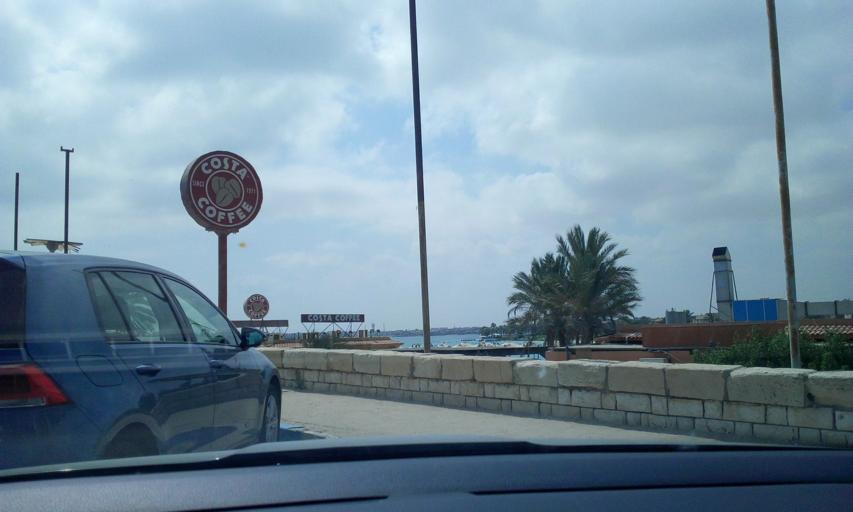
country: EG
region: Muhafazat Matruh
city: Al `Alamayn
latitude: 30.8439
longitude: 28.9761
